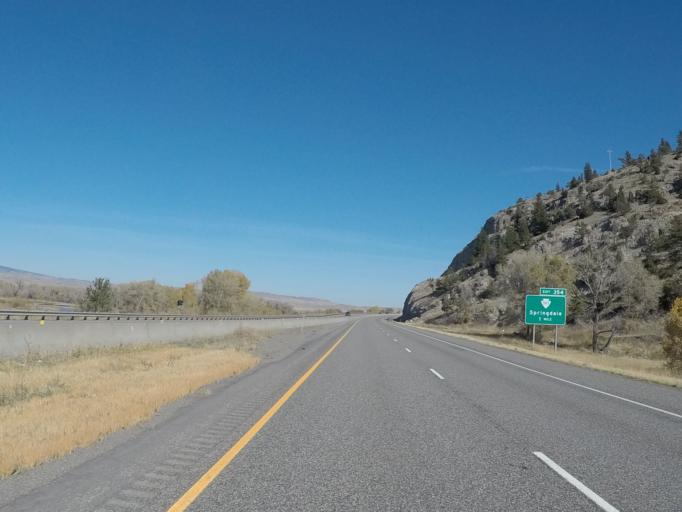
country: US
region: Montana
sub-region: Sweet Grass County
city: Big Timber
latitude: 45.7289
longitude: -110.2370
